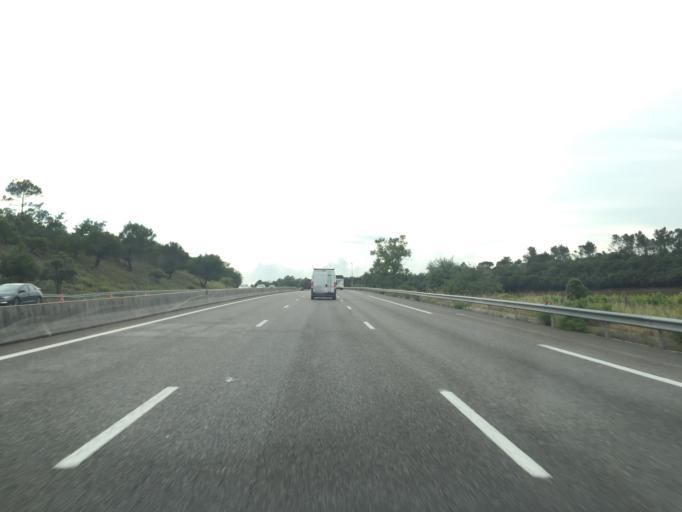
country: FR
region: Provence-Alpes-Cote d'Azur
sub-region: Departement du Var
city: Tourves
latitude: 43.4267
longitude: 5.9488
